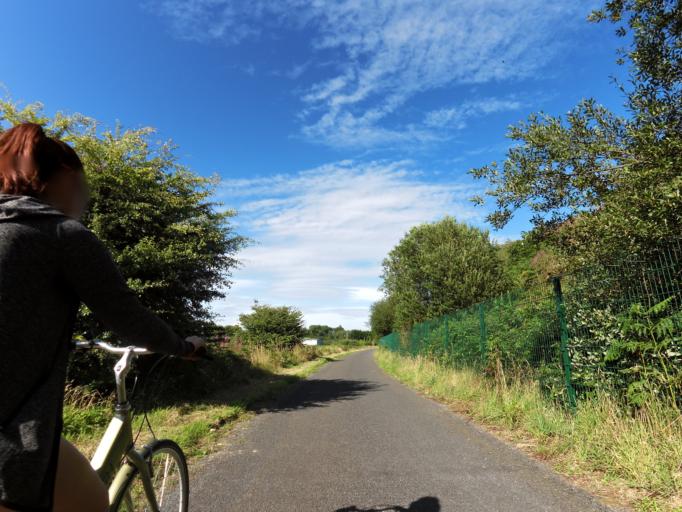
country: IE
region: Munster
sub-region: Waterford
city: Portlaw
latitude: 52.2238
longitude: -7.3413
